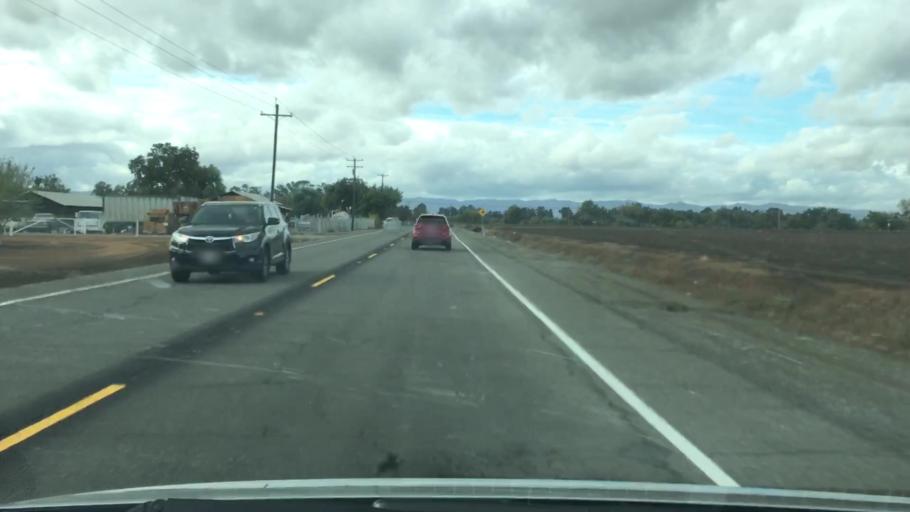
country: US
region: California
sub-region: Yolo County
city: Davis
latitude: 38.5616
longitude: -121.8374
